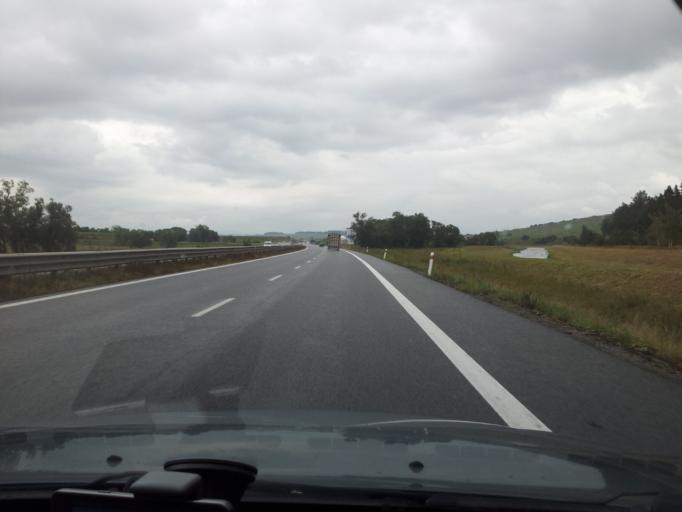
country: SK
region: Presovsky
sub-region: Okres Poprad
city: Poprad
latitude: 49.0903
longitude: 20.3374
